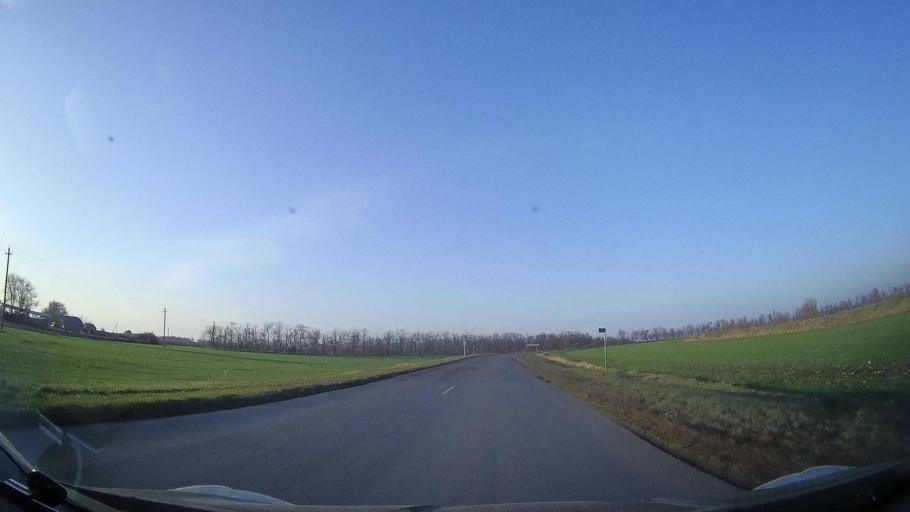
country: RU
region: Rostov
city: Kirovskaya
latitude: 47.0360
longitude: 39.9802
